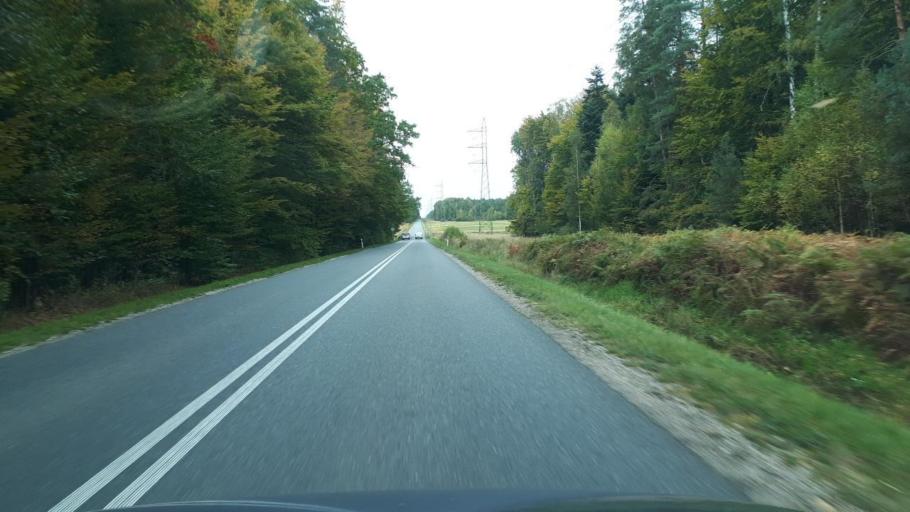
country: PL
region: Opole Voivodeship
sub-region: Powiat oleski
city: Dobrodzien
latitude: 50.7914
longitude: 18.4195
